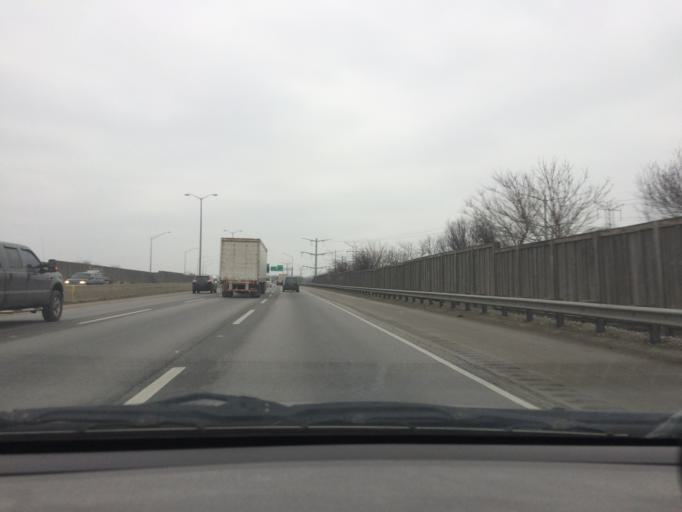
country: US
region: Illinois
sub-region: DuPage County
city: Glen Ellyn
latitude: 41.8675
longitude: -88.0390
